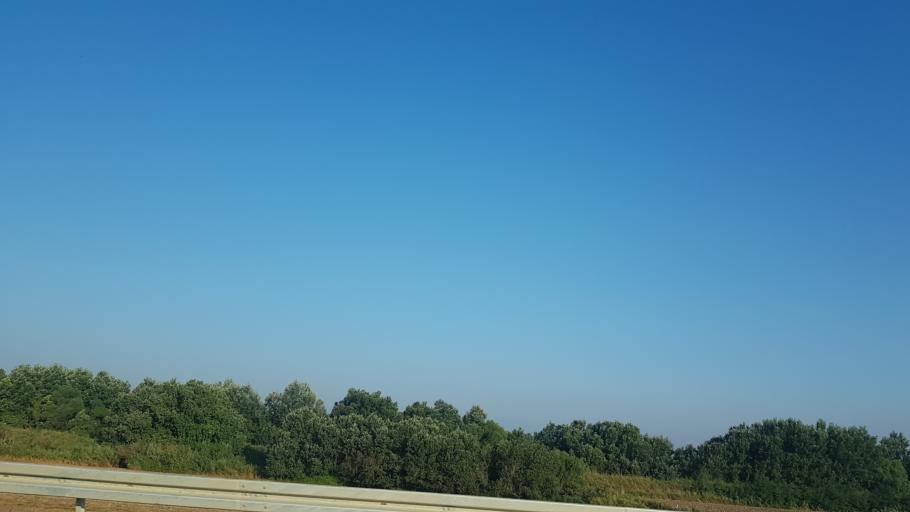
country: TR
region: Bursa
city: Karacabey
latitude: 40.1763
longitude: 28.3264
